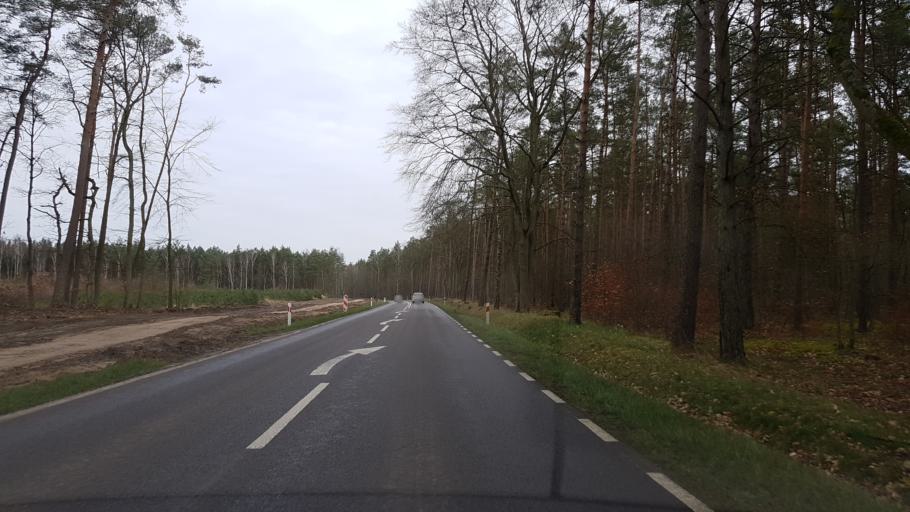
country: PL
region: West Pomeranian Voivodeship
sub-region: Powiat policki
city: Police
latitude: 53.6353
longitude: 14.5047
